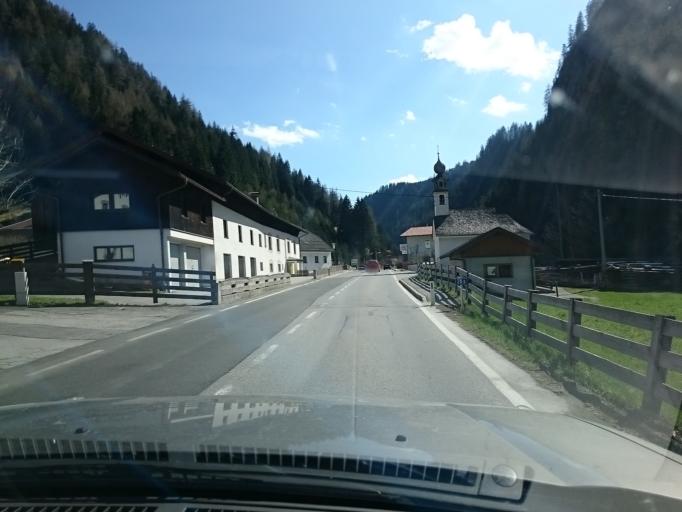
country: AT
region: Tyrol
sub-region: Politischer Bezirk Innsbruck Land
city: Gries am Brenner
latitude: 47.0646
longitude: 11.4882
